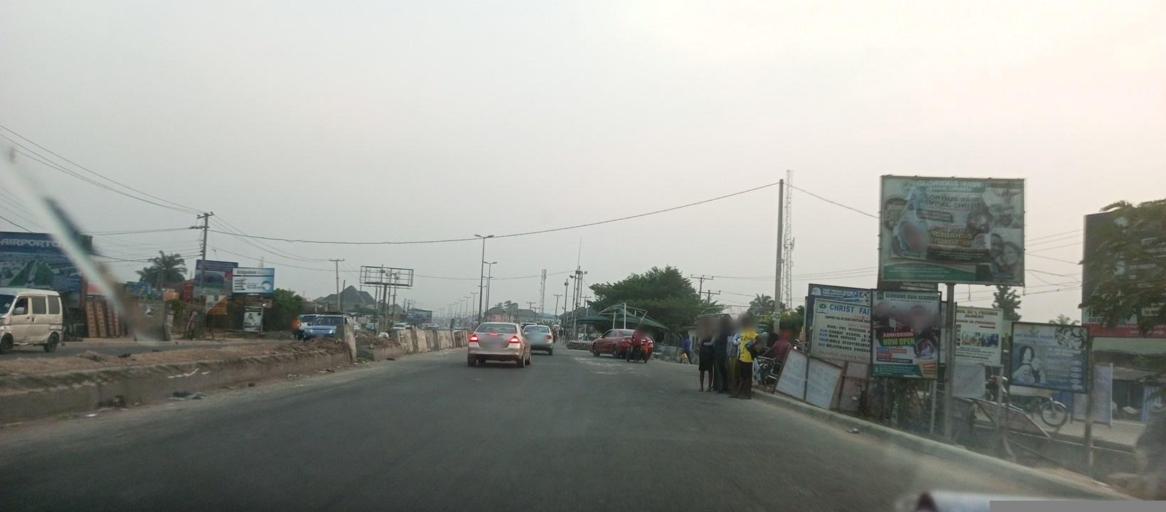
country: NG
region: Rivers
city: Emuoha
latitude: 4.9200
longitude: 6.9970
